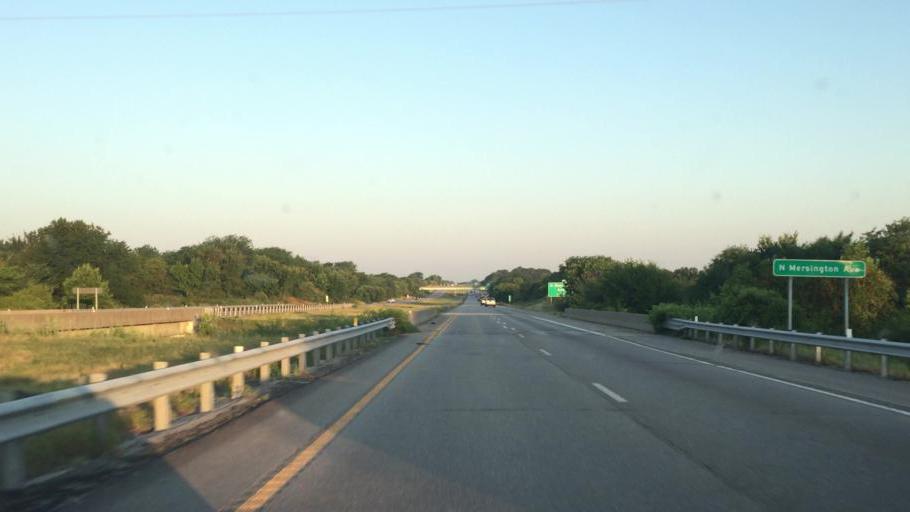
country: US
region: Missouri
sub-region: Clay County
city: Smithville
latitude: 39.3111
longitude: -94.5332
